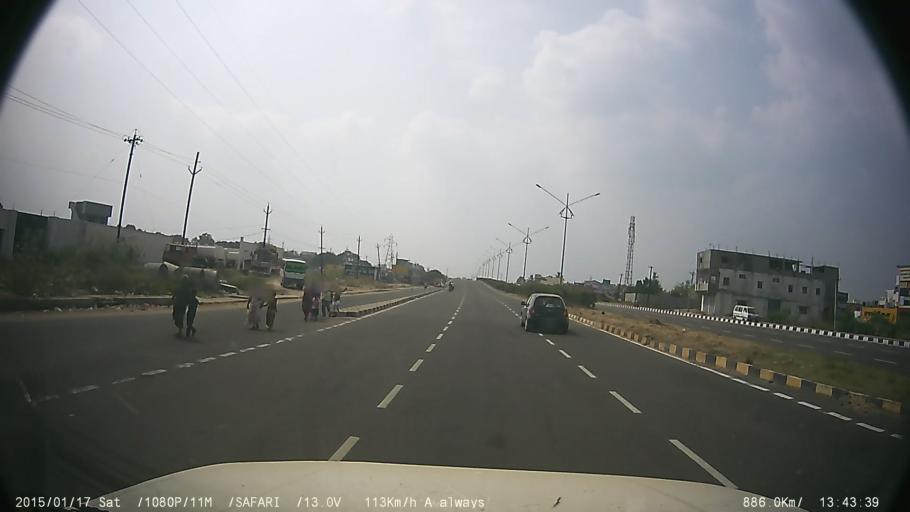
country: IN
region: Tamil Nadu
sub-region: Vellore
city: Vellore
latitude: 12.9261
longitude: 79.1206
